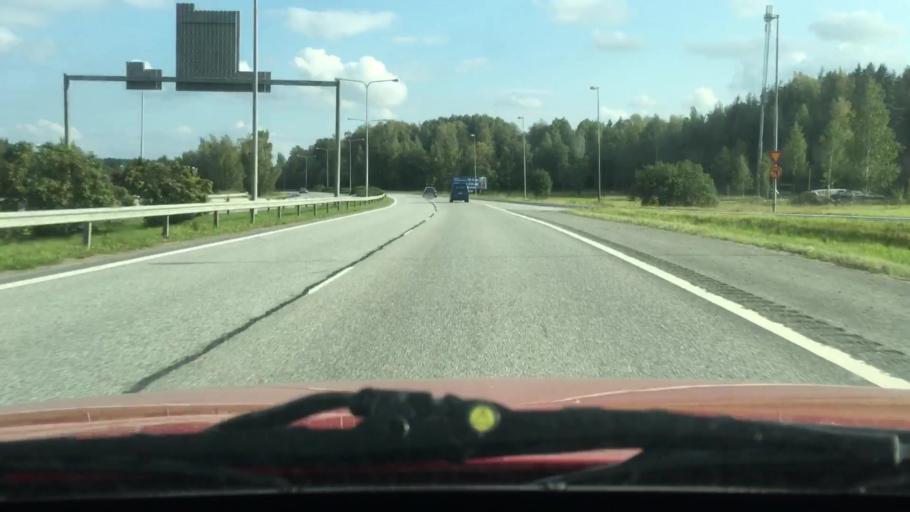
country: FI
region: Varsinais-Suomi
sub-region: Turku
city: Raisio
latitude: 60.4807
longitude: 22.1821
